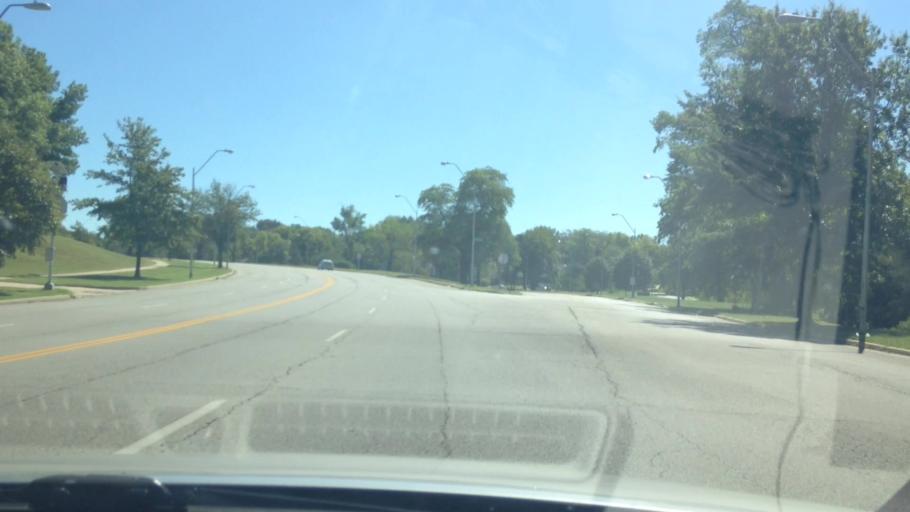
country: US
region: Kansas
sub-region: Johnson County
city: Mission Hills
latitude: 39.0105
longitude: -94.5679
